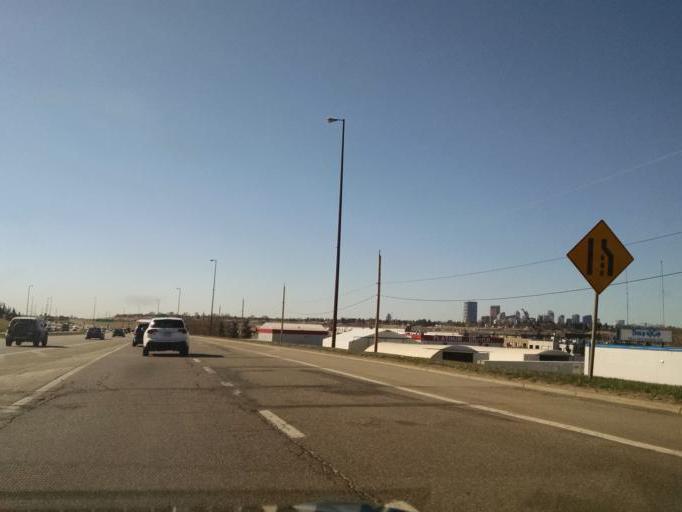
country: CA
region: Alberta
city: Calgary
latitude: 51.0914
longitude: -114.0399
